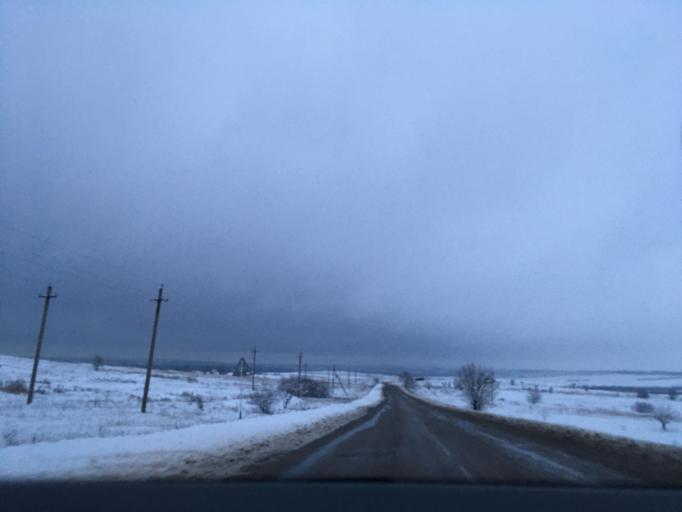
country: RU
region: Voronezj
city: Verkhniy Mamon
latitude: 50.0727
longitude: 40.2963
